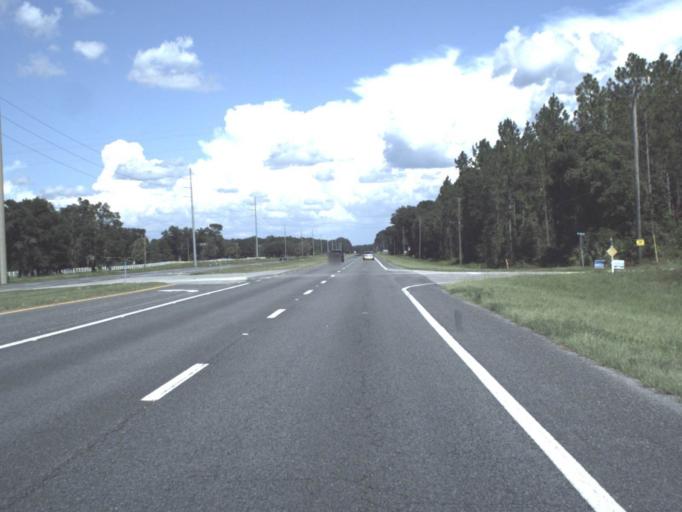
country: US
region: Florida
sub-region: Dixie County
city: Cross City
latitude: 29.6054
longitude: -83.0423
